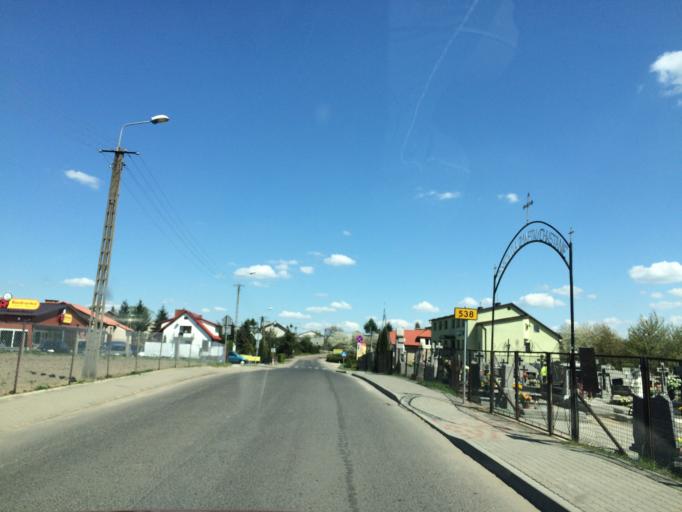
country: PL
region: Warmian-Masurian Voivodeship
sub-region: Powiat ilawski
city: Lubawa
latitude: 53.4123
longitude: 19.7620
